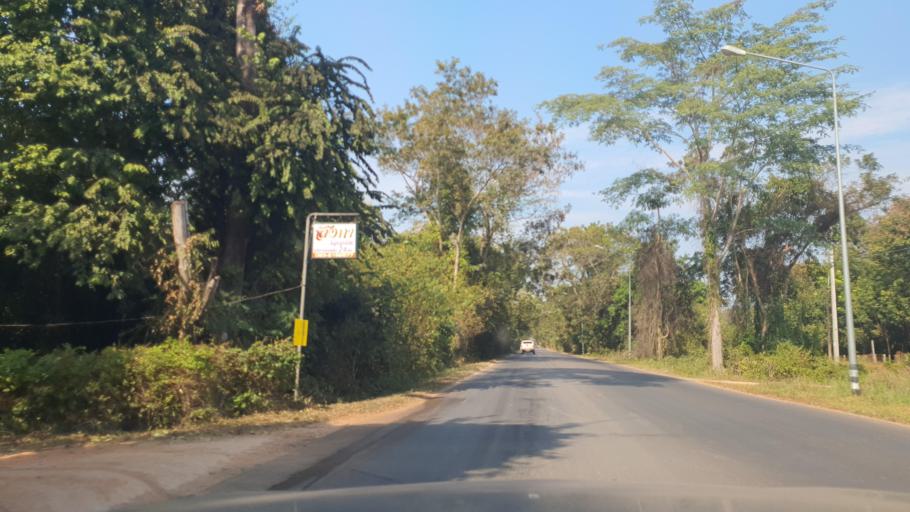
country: TH
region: Nakhon Phanom
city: Ban Phaeng
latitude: 18.0177
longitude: 104.1533
